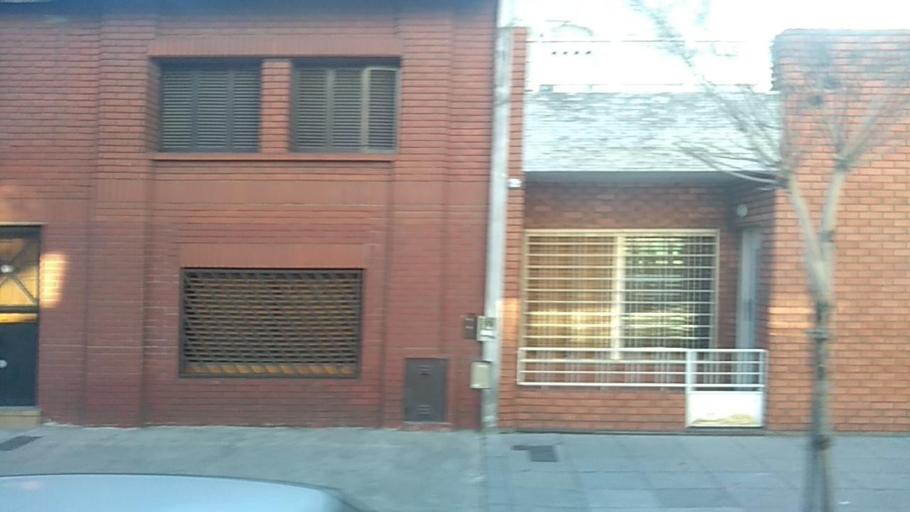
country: AR
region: Buenos Aires F.D.
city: Villa Santa Rita
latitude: -34.6211
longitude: -58.5100
